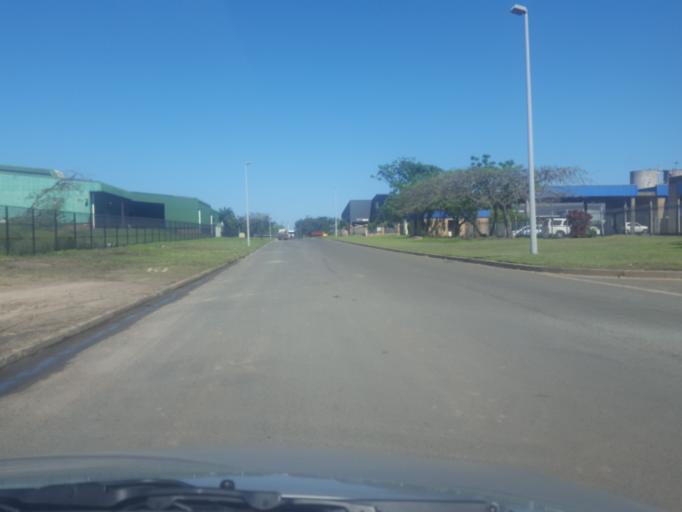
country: ZA
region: KwaZulu-Natal
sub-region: uThungulu District Municipality
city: Richards Bay
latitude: -28.7563
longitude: 32.0136
